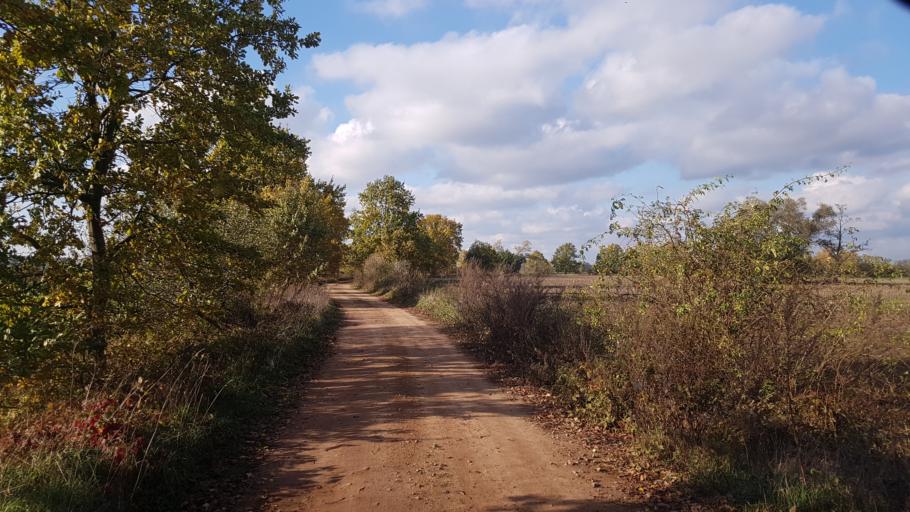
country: DE
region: Brandenburg
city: Schonewalde
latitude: 51.6813
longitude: 13.5844
